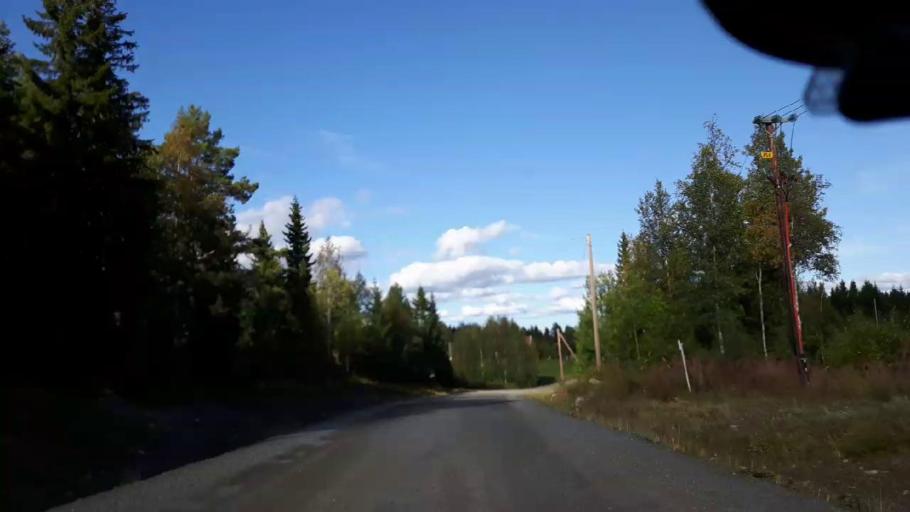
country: SE
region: Jaemtland
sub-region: Ragunda Kommun
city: Hammarstrand
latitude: 63.4325
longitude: 16.1810
